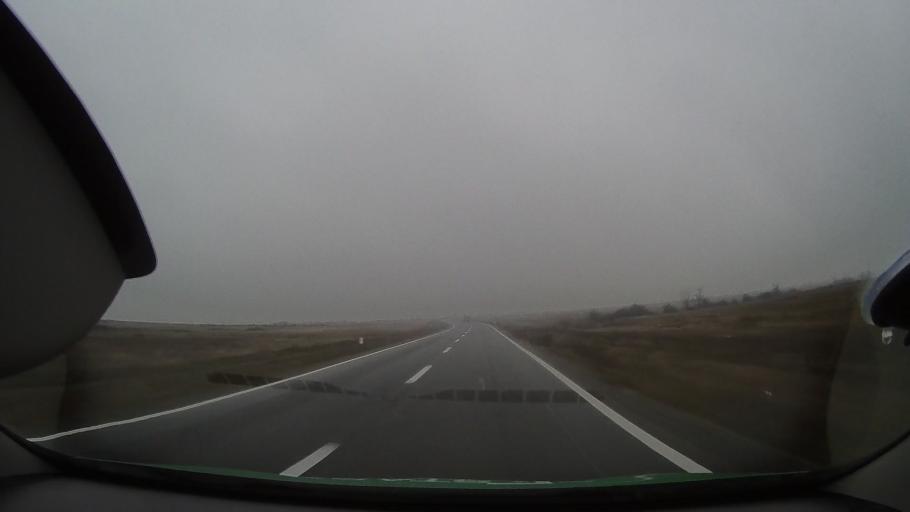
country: RO
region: Arad
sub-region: Comuna Craiova
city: Craiova
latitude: 46.6246
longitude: 21.9585
